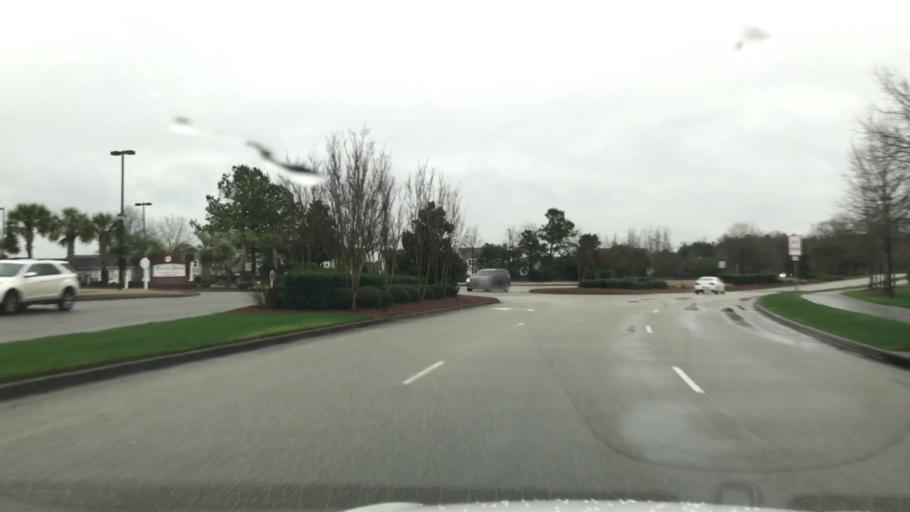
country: US
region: South Carolina
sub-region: Horry County
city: Myrtle Beach
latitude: 33.7374
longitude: -78.8971
